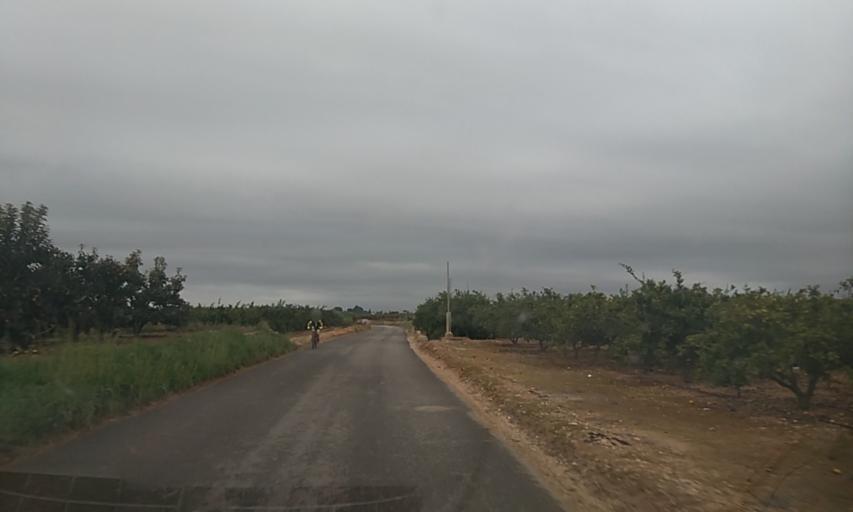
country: ES
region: Valencia
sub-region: Provincia de Valencia
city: Benimodo
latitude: 39.1887
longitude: -0.5312
